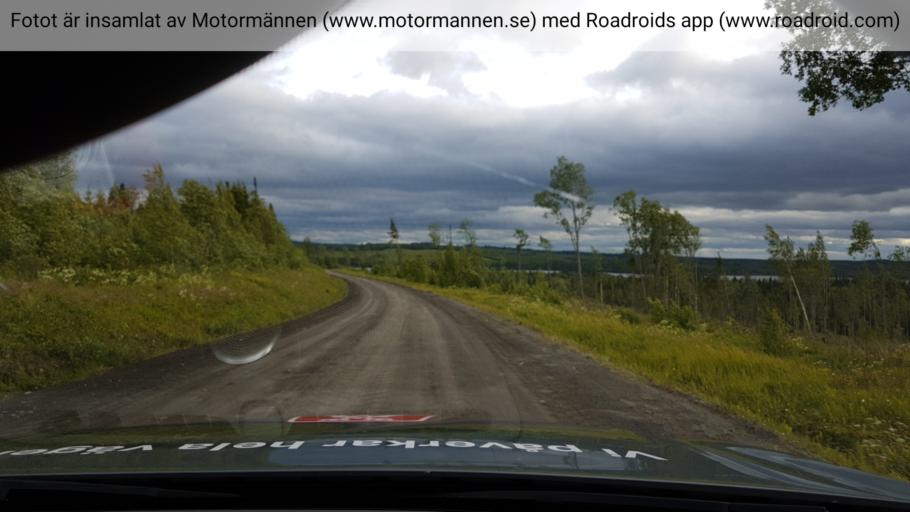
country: SE
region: Jaemtland
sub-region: OEstersunds Kommun
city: Lit
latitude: 63.5949
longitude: 14.9866
